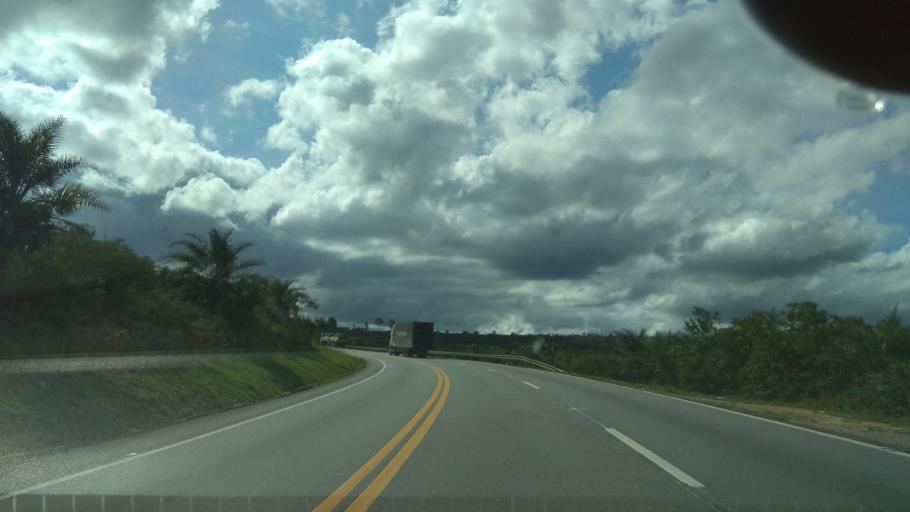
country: BR
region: Bahia
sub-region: Santa Ines
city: Santa Ines
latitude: -13.1172
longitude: -39.9893
